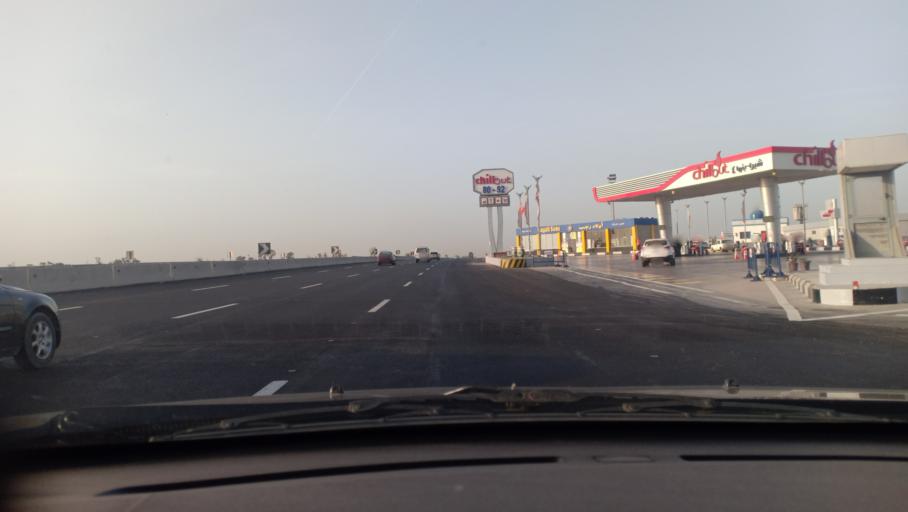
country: EG
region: Muhafazat al Qalyubiyah
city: Toukh
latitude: 30.3043
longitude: 31.2201
